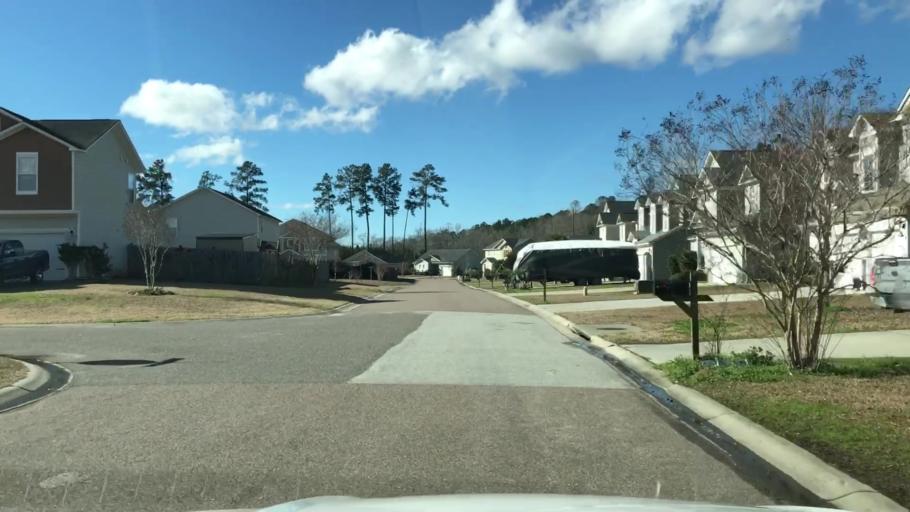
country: US
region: South Carolina
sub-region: Dorchester County
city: Summerville
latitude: 33.0909
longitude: -80.1952
